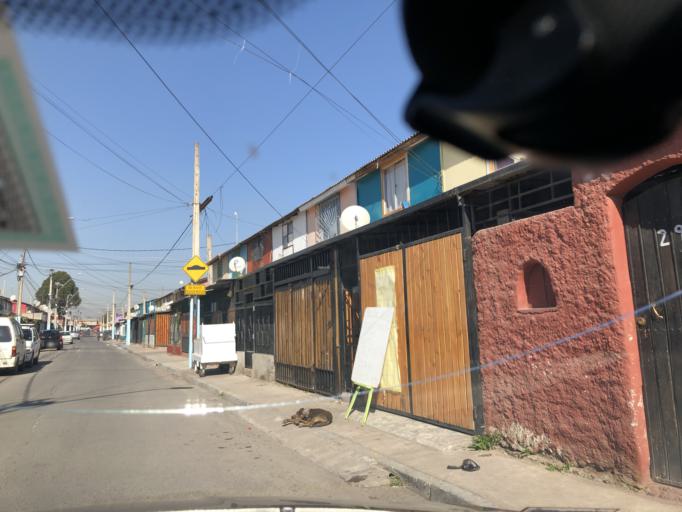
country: CL
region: Santiago Metropolitan
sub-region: Provincia de Santiago
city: La Pintana
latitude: -33.5869
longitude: -70.6064
